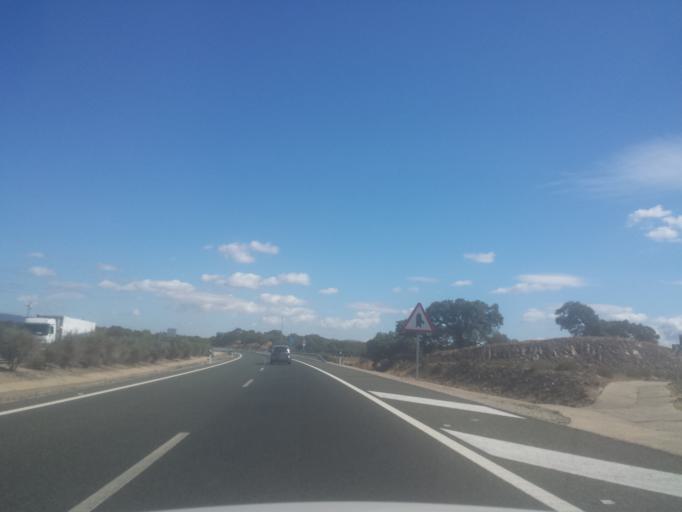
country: ES
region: Andalusia
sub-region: Provincia de Huelva
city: Santa Olalla del Cala
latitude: 37.9035
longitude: -6.2134
